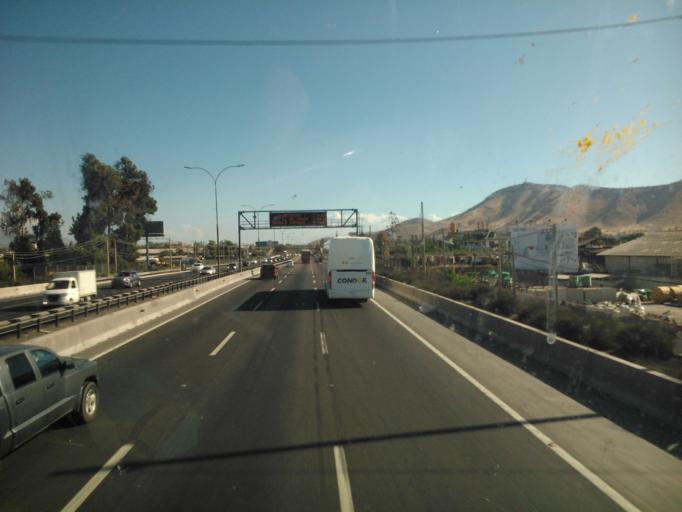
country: CL
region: Santiago Metropolitan
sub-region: Provincia de Maipo
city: San Bernardo
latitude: -33.5673
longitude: -70.7118
